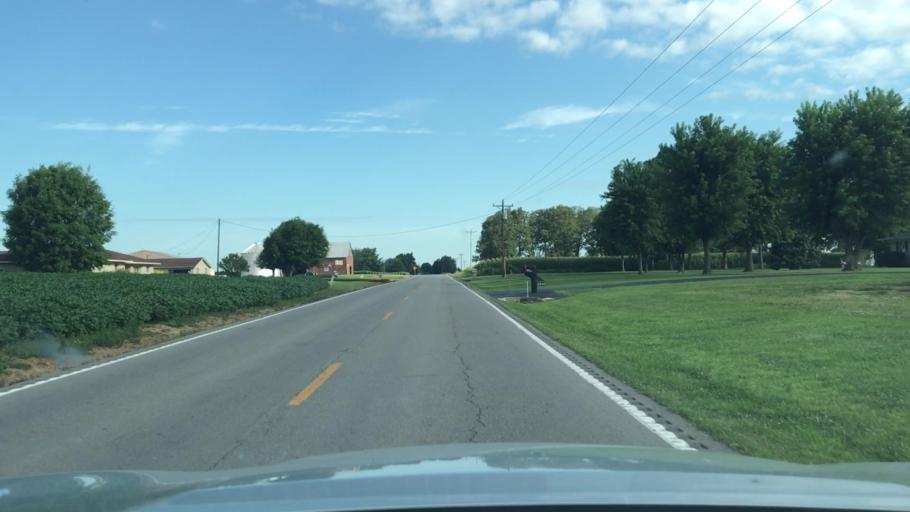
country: US
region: Kentucky
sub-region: Todd County
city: Elkton
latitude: 36.8696
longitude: -87.1640
